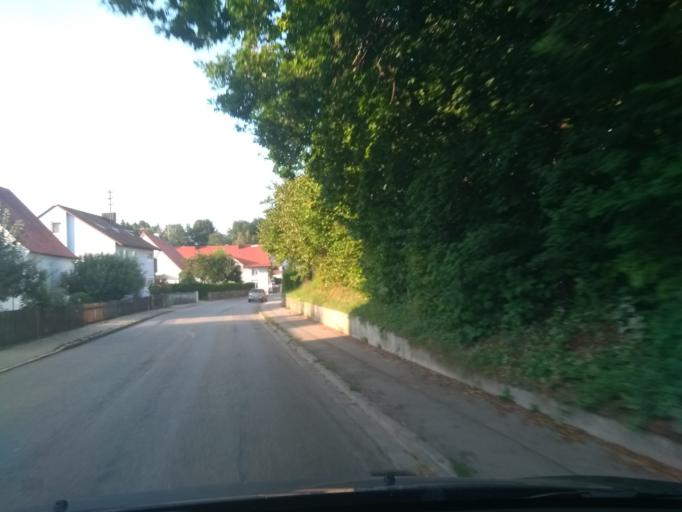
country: DE
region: Bavaria
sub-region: Upper Bavaria
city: Markt Indersdorf
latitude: 48.3247
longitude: 11.3880
